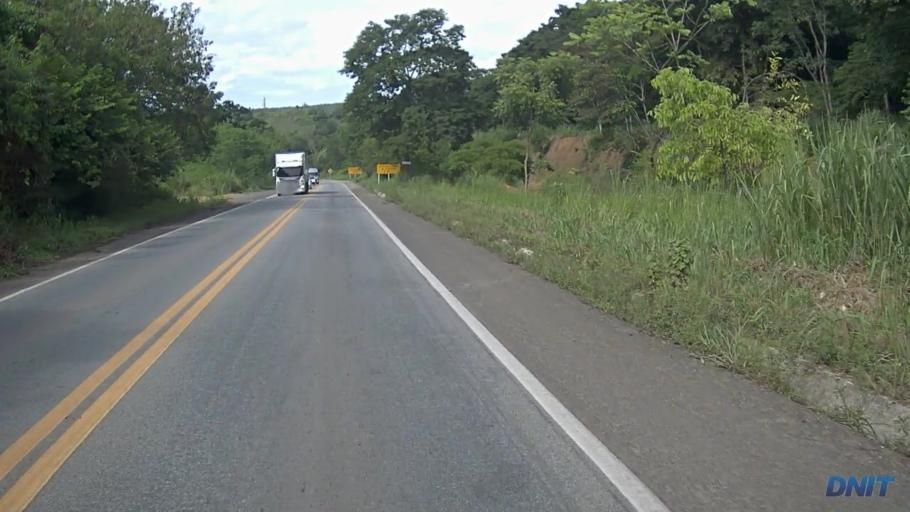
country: BR
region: Minas Gerais
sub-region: Ipaba
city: Ipaba
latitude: -19.3392
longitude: -42.4278
